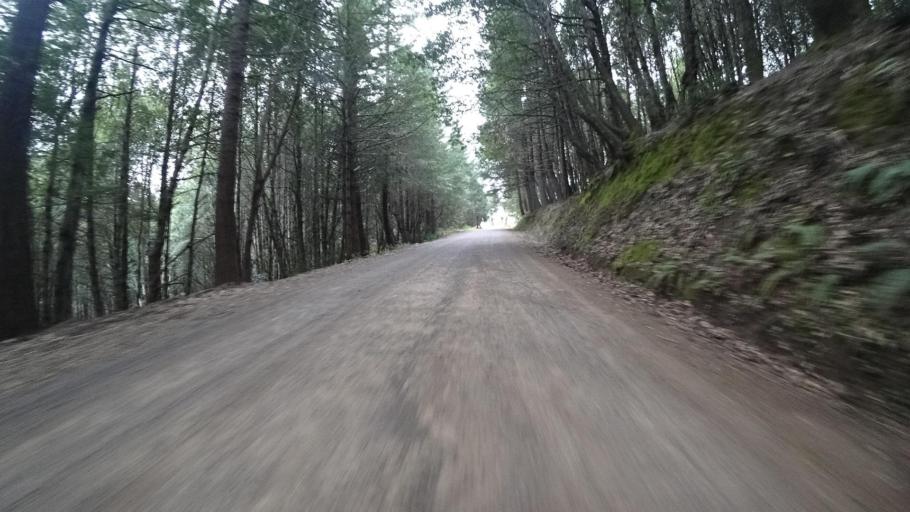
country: US
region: California
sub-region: Humboldt County
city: Redway
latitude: 40.2211
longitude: -123.7560
